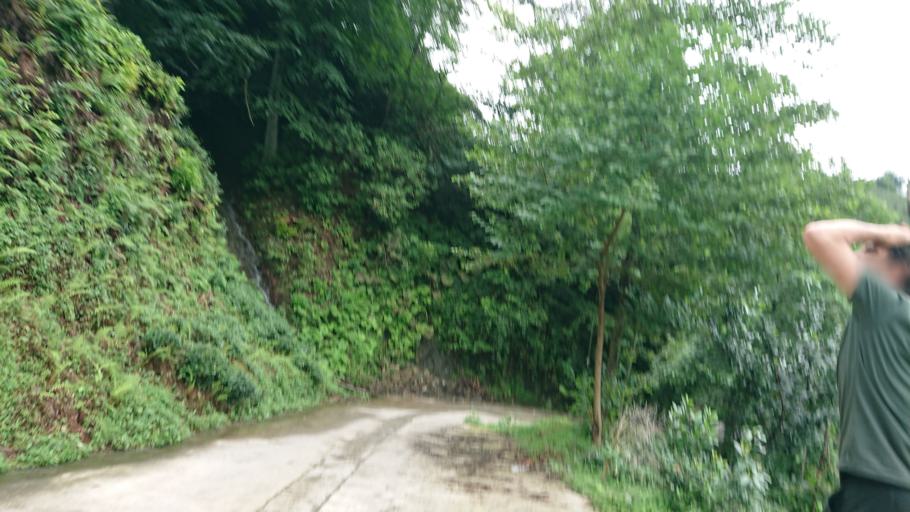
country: TR
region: Rize
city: Rize
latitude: 40.9764
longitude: 40.4857
